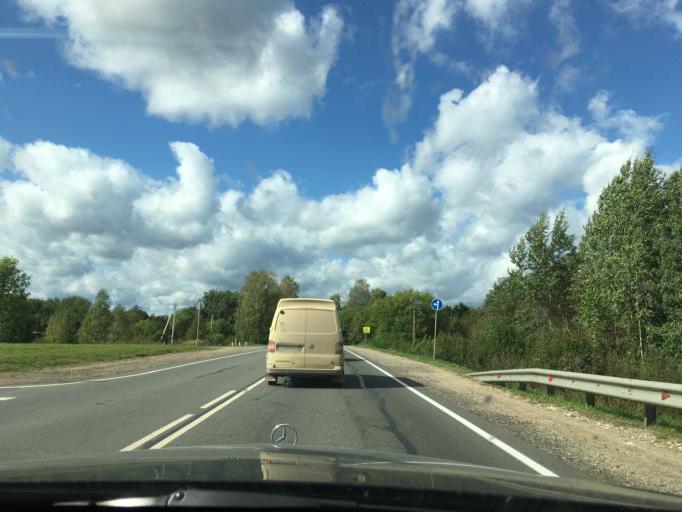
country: RU
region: Pskov
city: Pustoshka
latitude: 56.4008
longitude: 29.2317
